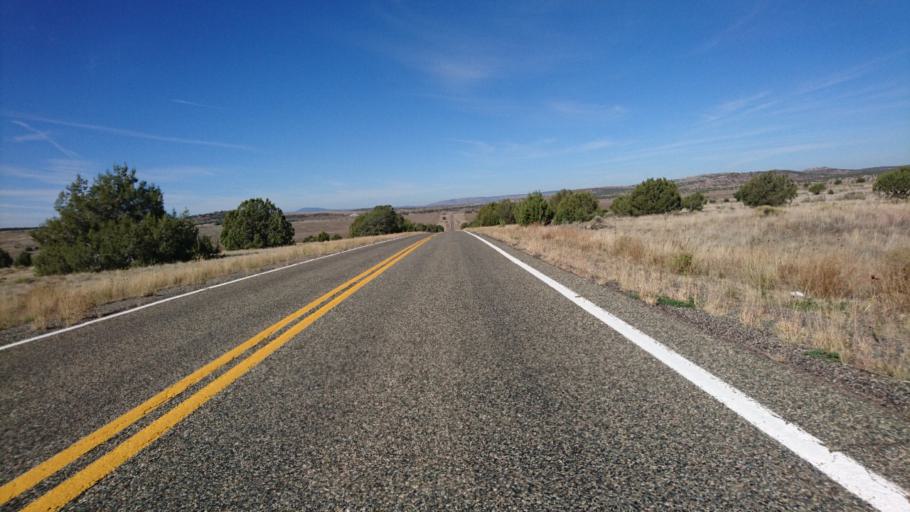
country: US
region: Arizona
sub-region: Yavapai County
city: Paulden
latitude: 35.2823
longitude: -112.7114
